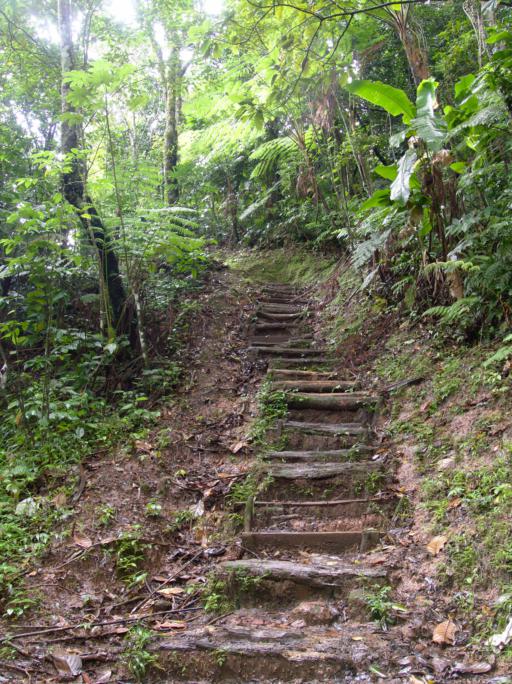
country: MQ
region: Martinique
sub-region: Martinique
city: Saint-Joseph
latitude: 14.6770
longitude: -61.0959
